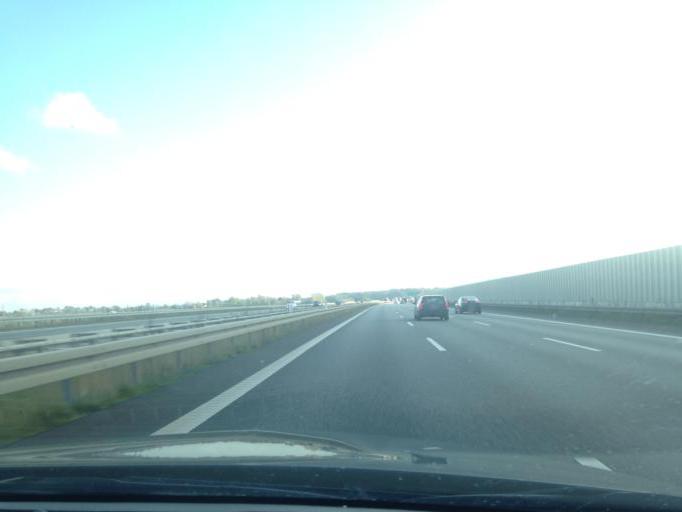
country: DK
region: South Denmark
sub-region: Vejle Kommune
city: Borkop
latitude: 55.6220
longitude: 9.5731
